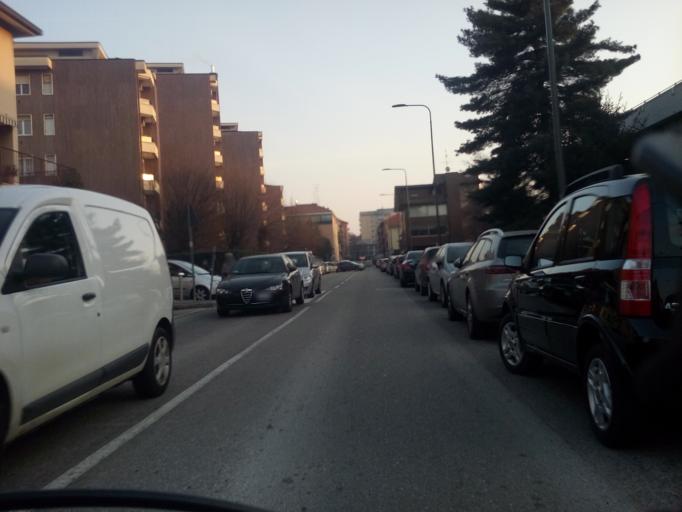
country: IT
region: Lombardy
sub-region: Citta metropolitana di Milano
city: Cesano Boscone
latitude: 45.4609
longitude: 9.0875
